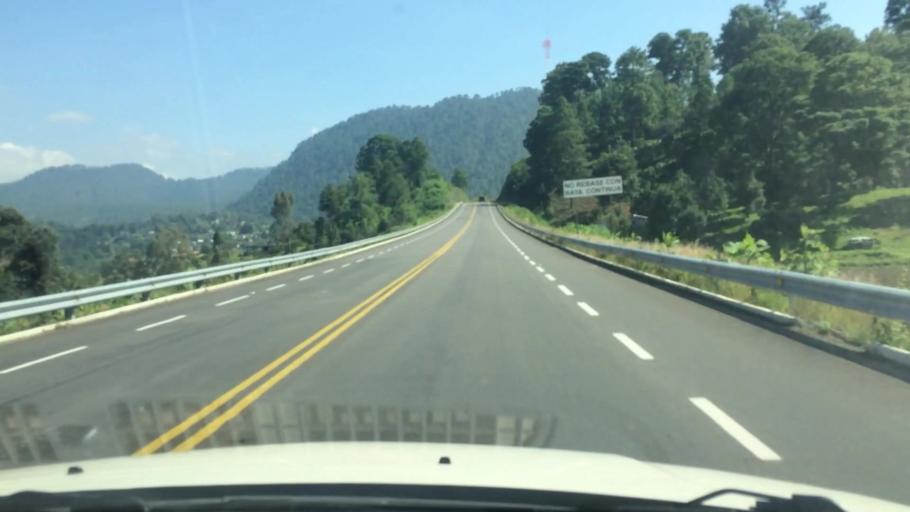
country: MX
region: Mexico
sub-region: Amanalco
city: Polvillos (San Bartolo Quinta Seccion)
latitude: 19.2244
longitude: -100.0849
